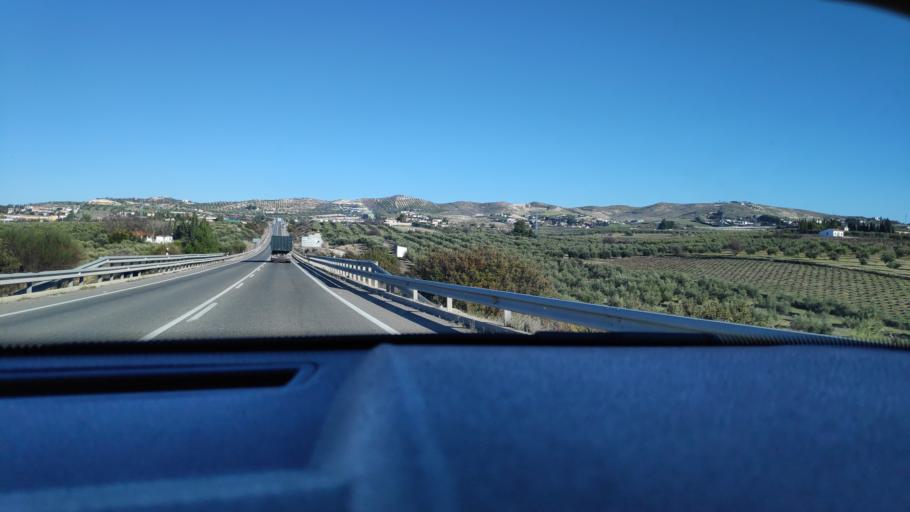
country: ES
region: Andalusia
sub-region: Province of Cordoba
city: Baena
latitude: 37.6136
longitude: -4.3008
